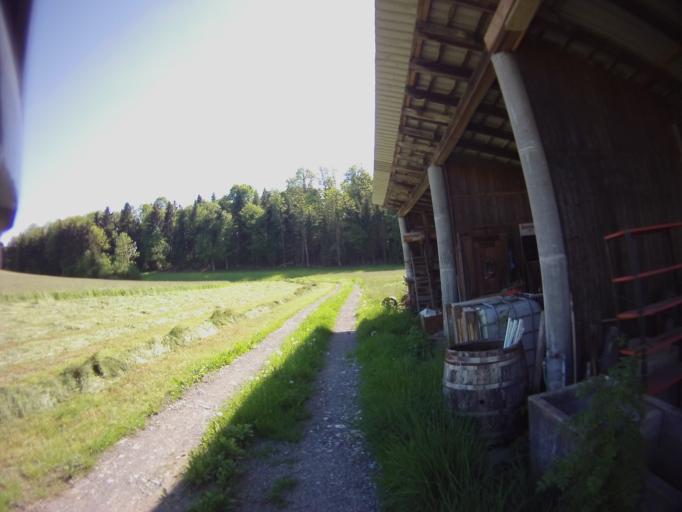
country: CH
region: Zurich
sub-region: Bezirk Affoltern
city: Knonau
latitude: 47.2089
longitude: 8.4460
